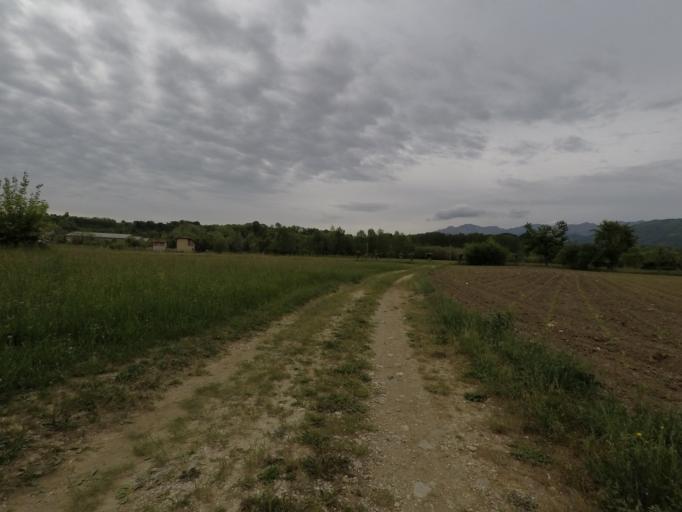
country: IT
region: Friuli Venezia Giulia
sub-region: Provincia di Udine
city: Nimis
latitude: 46.1846
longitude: 13.2505
